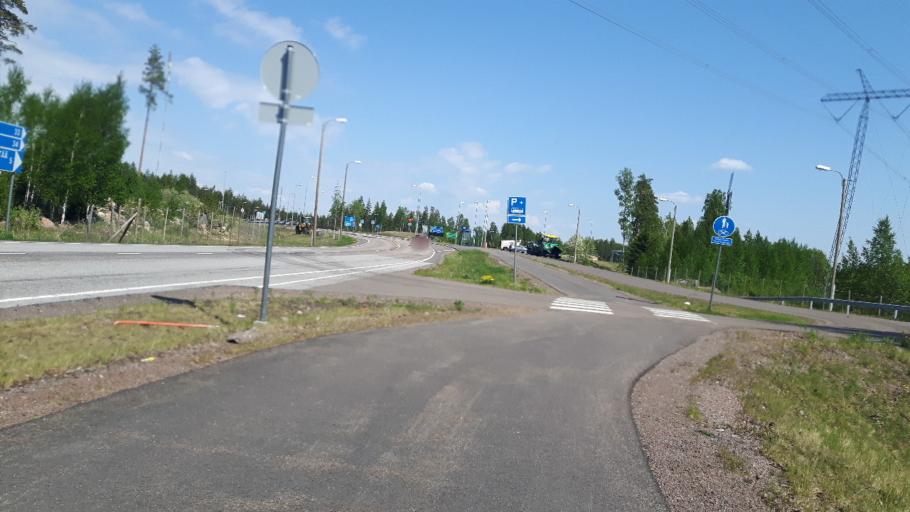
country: FI
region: Uusimaa
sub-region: Loviisa
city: Ruotsinpyhtaeae
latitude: 60.4901
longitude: 26.4177
